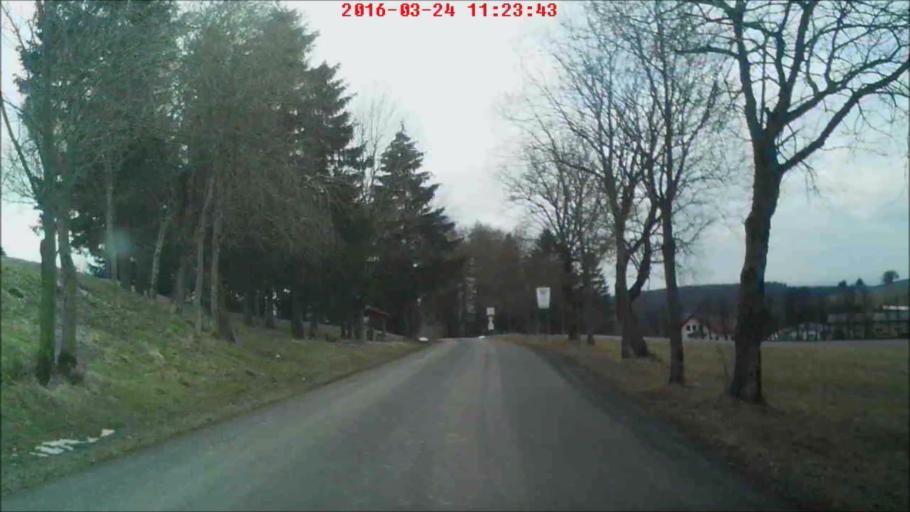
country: DE
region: Thuringia
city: Eisfeld
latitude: 50.4775
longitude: 10.9233
